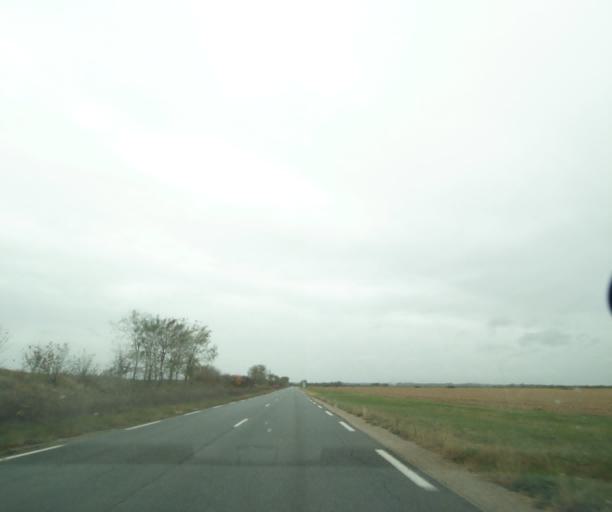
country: FR
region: Rhone-Alpes
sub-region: Departement de l'Ain
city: Loyettes
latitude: 45.7920
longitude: 5.2439
